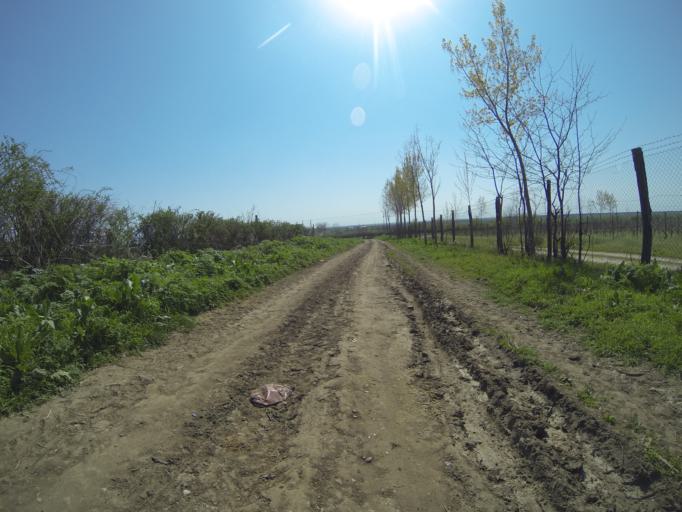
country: RO
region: Dolj
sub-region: Comuna Segarcea
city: Segarcea
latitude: 44.1011
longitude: 23.7255
